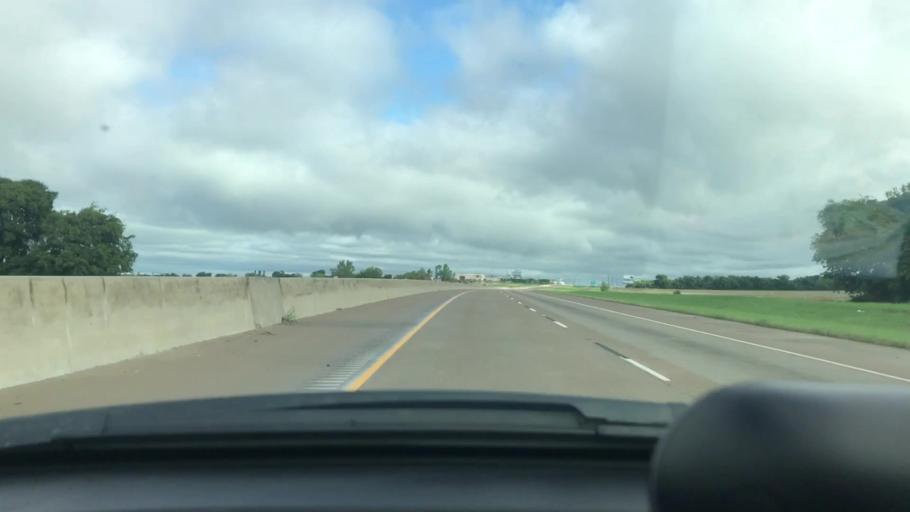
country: US
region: Texas
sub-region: Grayson County
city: Howe
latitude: 33.4794
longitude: -96.6193
